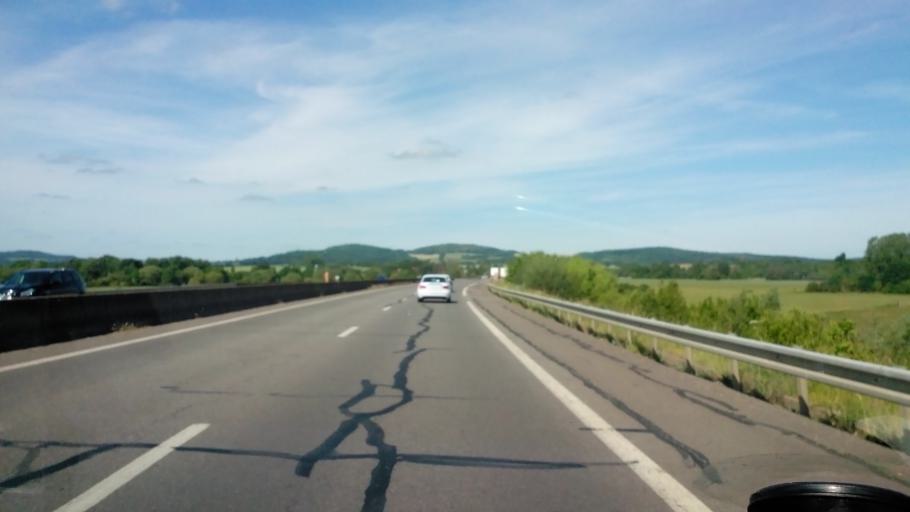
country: FR
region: Lorraine
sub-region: Departement de la Moselle
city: Marly
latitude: 49.0510
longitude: 6.1630
